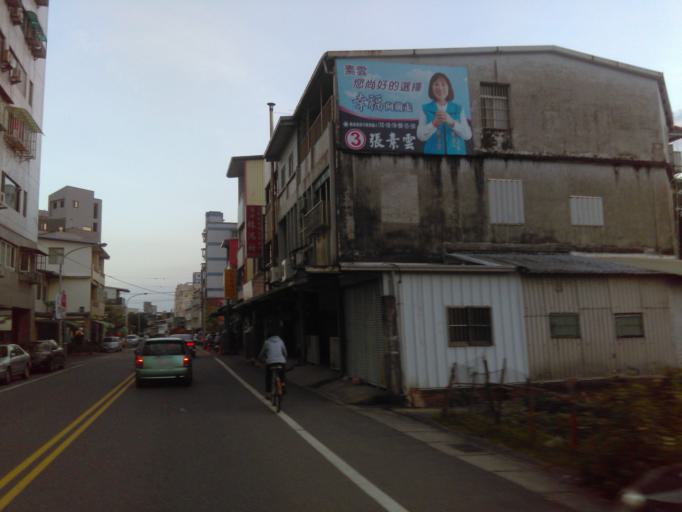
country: TW
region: Taiwan
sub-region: Yilan
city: Yilan
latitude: 24.8210
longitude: 121.7664
